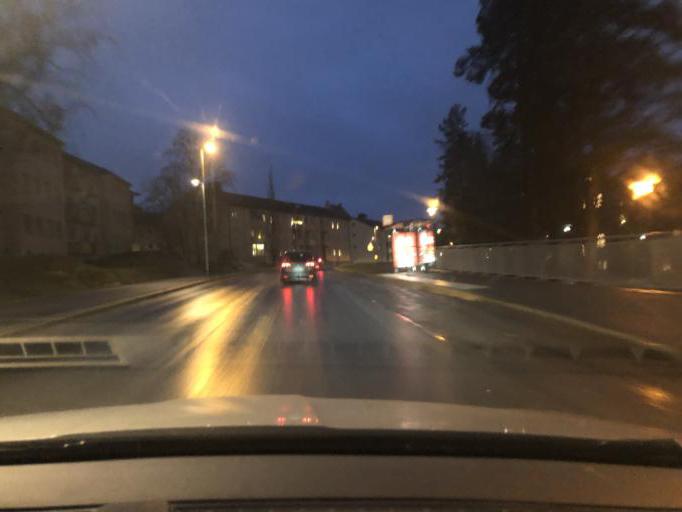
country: SE
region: Vaermland
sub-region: Karlstads Kommun
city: Karlstad
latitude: 59.3757
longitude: 13.4822
